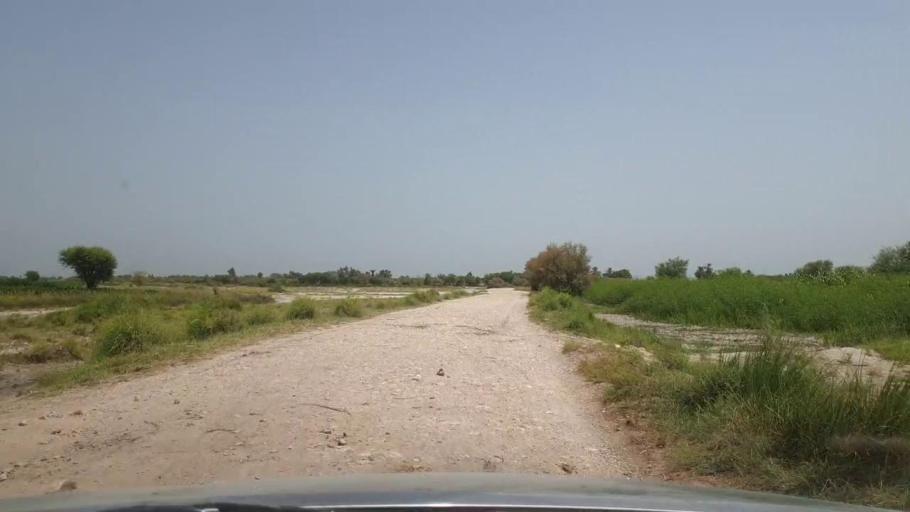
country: PK
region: Sindh
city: Pano Aqil
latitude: 27.8679
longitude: 69.1778
